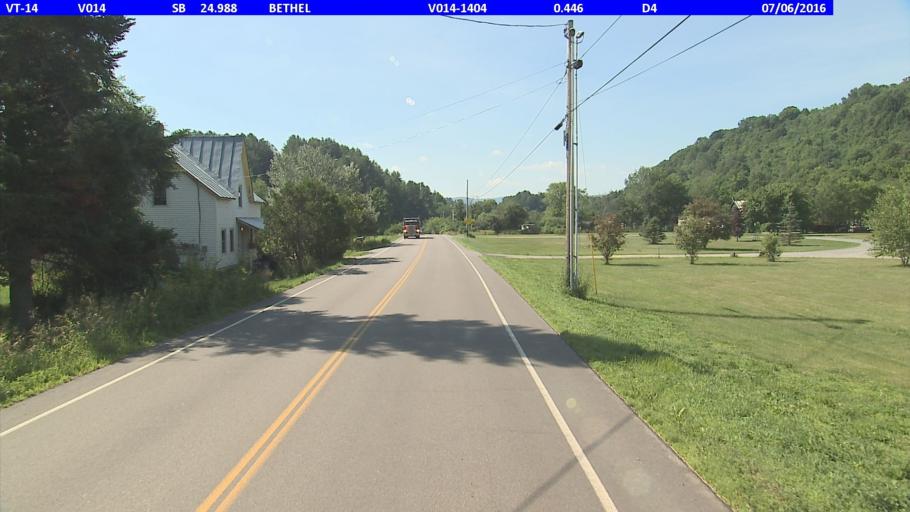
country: US
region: Vermont
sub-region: Orange County
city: Randolph
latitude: 43.8696
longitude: -72.5838
